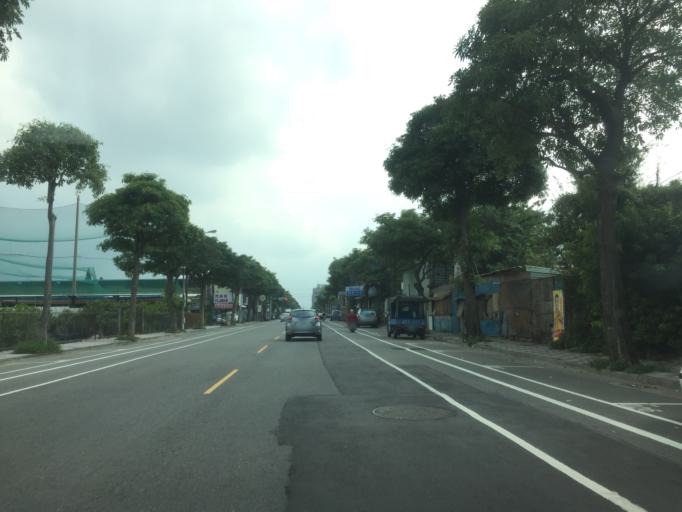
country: TW
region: Taiwan
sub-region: Taoyuan
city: Taoyuan
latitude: 24.9712
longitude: 121.3068
